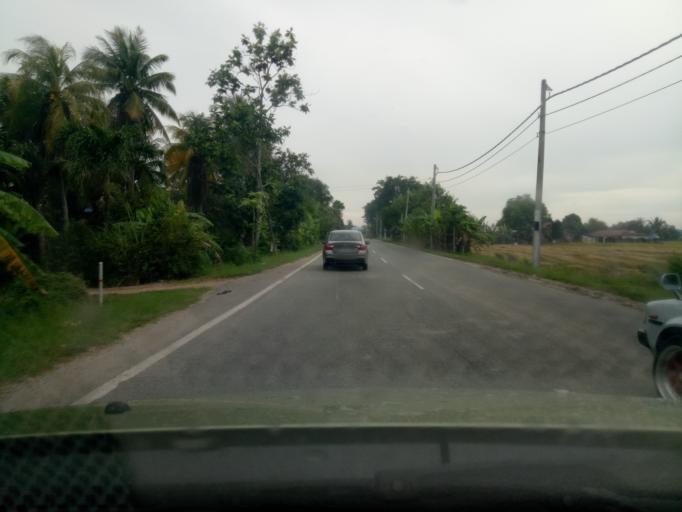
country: MY
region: Kedah
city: Alor Setar
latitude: 5.9730
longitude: 100.4094
